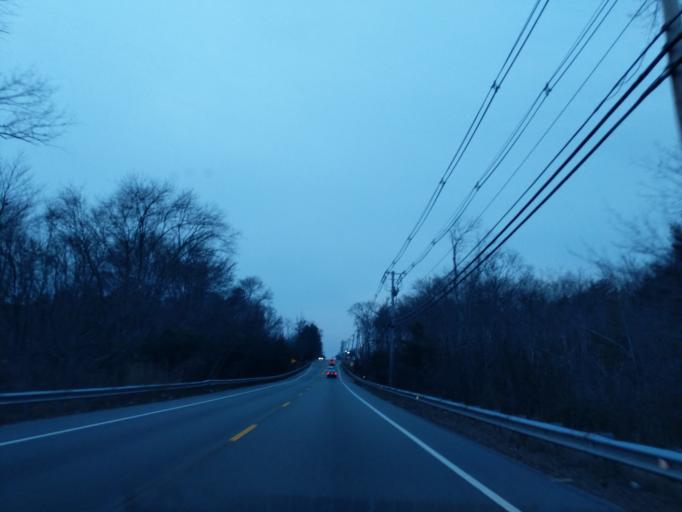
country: US
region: Massachusetts
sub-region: Bristol County
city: Raynham Center
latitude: 41.9048
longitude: -71.0192
